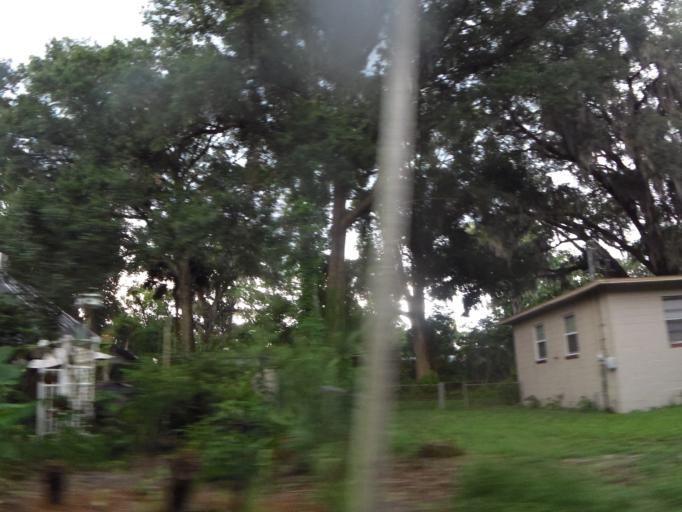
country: US
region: Florida
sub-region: Duval County
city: Jacksonville
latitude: 30.3435
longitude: -81.6053
